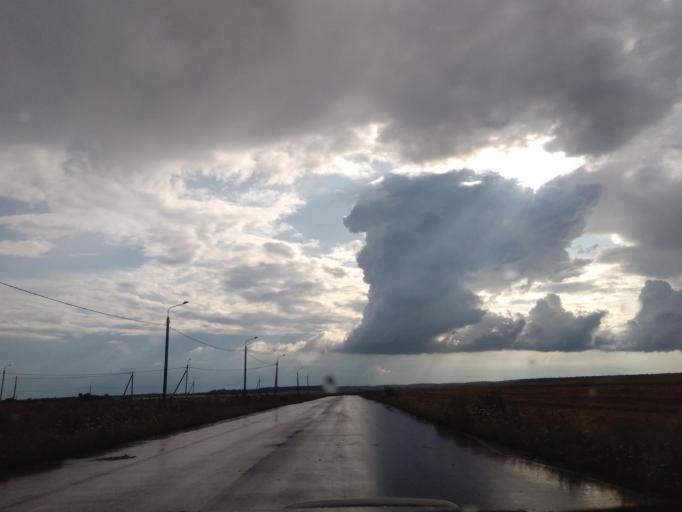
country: BY
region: Minsk
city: Kapyl'
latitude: 53.1674
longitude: 27.0785
